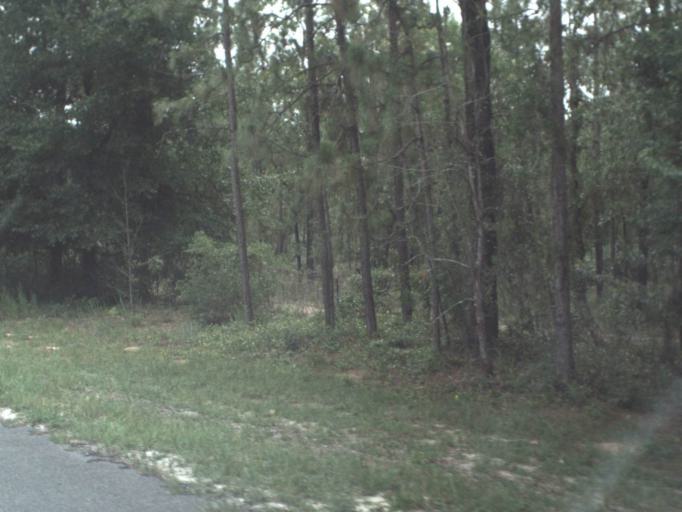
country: US
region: Florida
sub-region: Clay County
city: Keystone Heights
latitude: 29.8512
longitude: -81.9581
